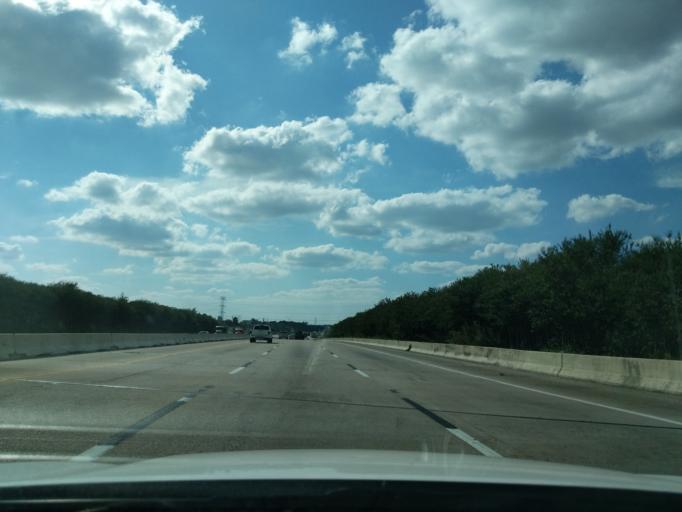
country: US
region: Texas
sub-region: Chambers County
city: Mont Belvieu
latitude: 29.8216
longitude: -94.8994
